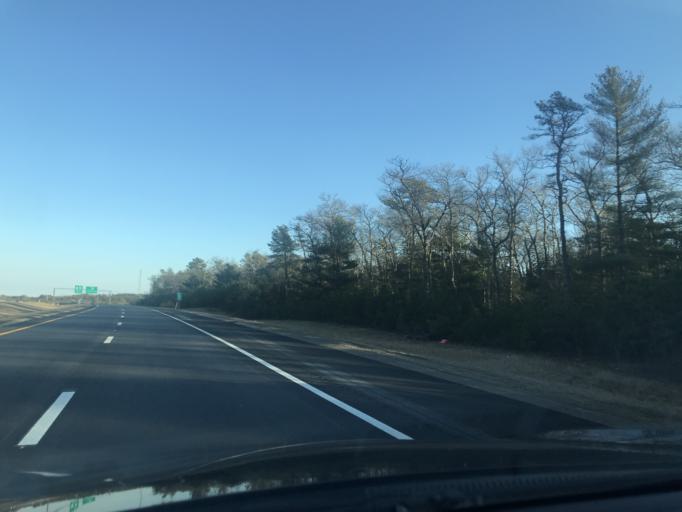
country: US
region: Massachusetts
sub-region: Plymouth County
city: Kingston
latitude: 41.9581
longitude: -70.7213
